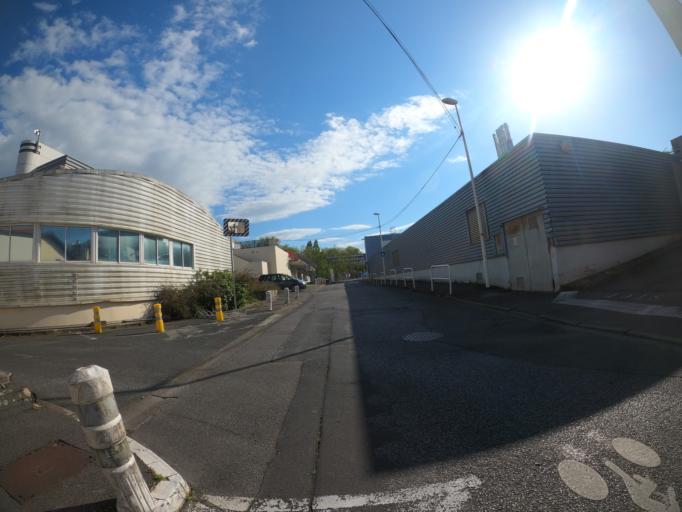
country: FR
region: Aquitaine
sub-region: Departement des Pyrenees-Atlantiques
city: Bayonne
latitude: 43.4825
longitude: -1.4786
